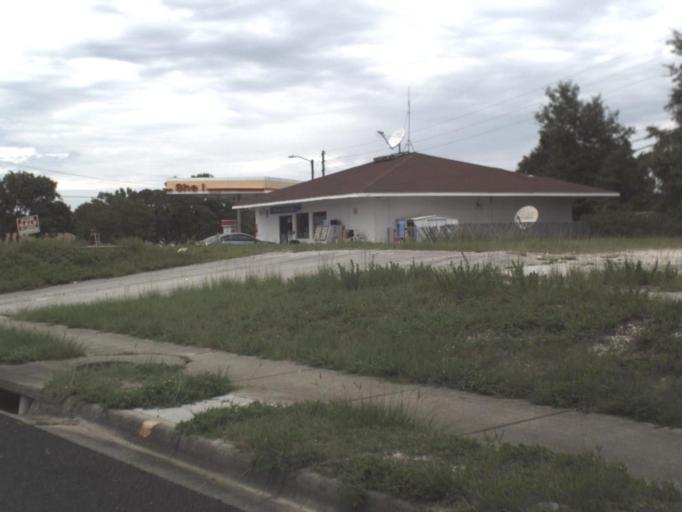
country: US
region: Florida
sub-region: Citrus County
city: Inverness Highlands North
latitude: 28.8435
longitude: -82.3650
